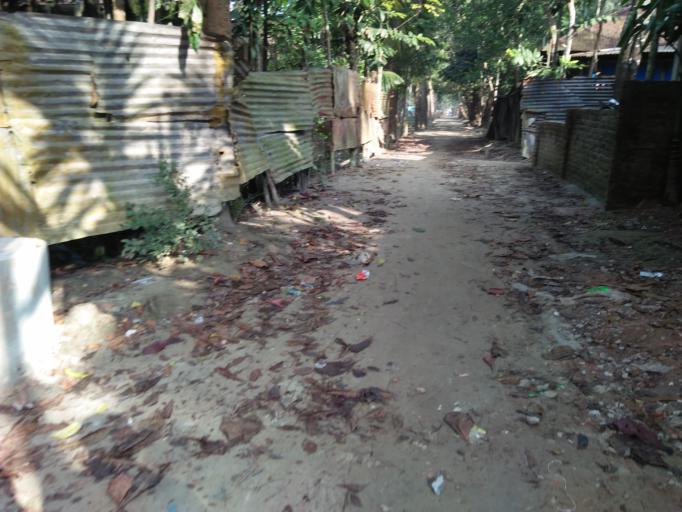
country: BD
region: Barisal
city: Bhola
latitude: 22.6769
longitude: 90.6400
